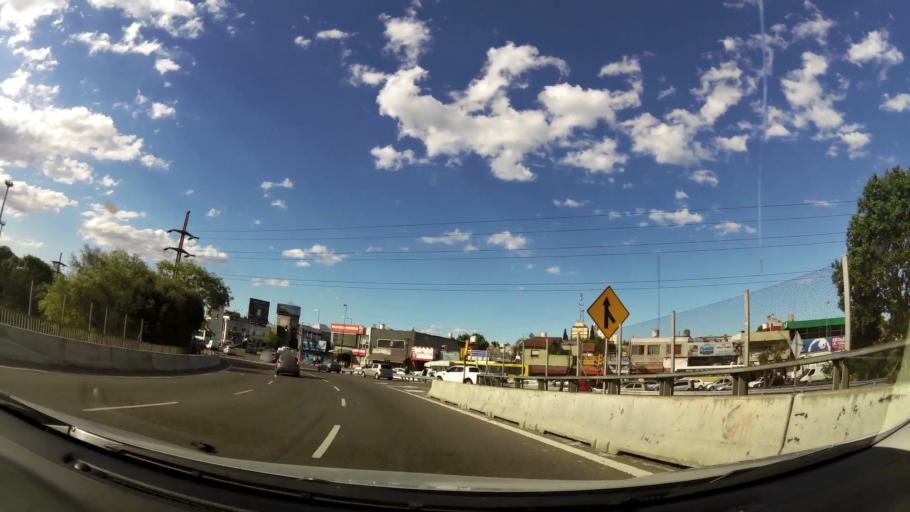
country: AR
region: Buenos Aires
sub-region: Partido de San Isidro
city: San Isidro
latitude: -34.4966
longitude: -58.5528
